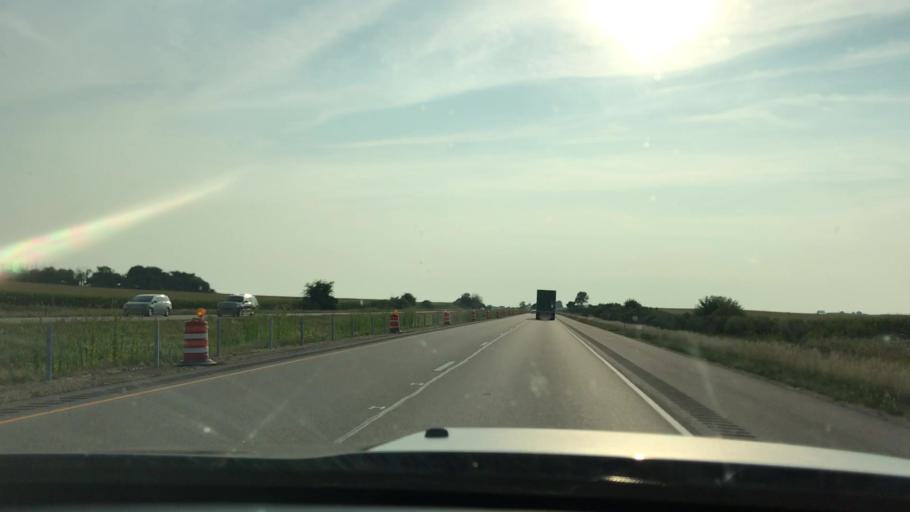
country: US
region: Illinois
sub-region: Bureau County
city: Walnut
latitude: 41.3942
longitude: -89.6296
